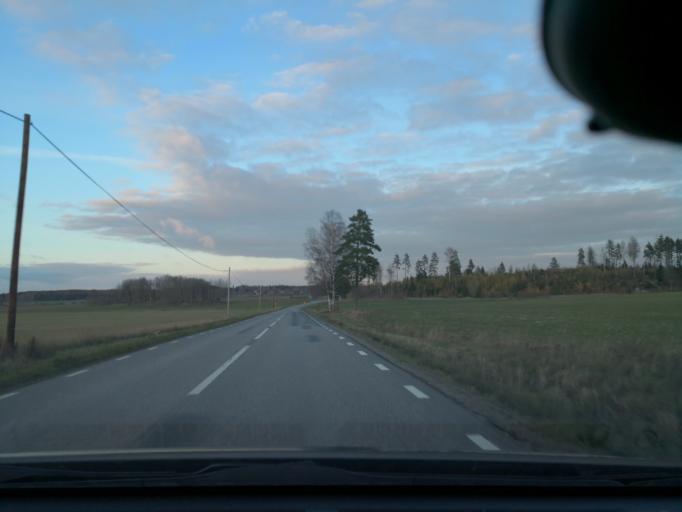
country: SE
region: Vaestmanland
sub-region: Vasteras
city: Tillberga
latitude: 59.6620
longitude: 16.7014
